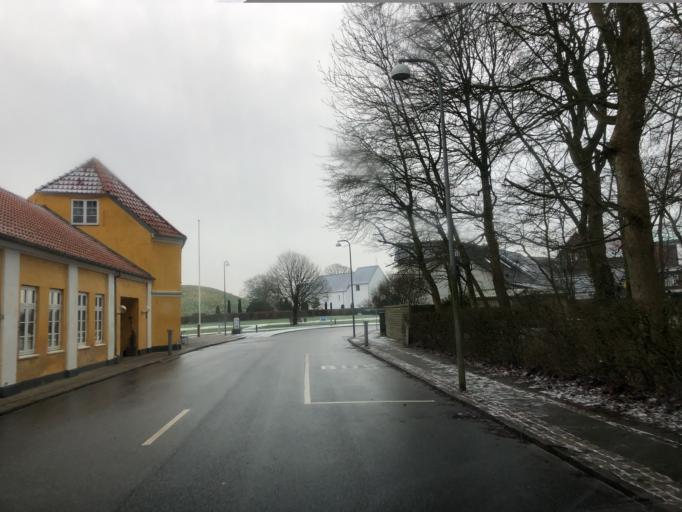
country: DK
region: South Denmark
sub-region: Vejle Kommune
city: Jelling
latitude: 55.7579
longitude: 9.4180
